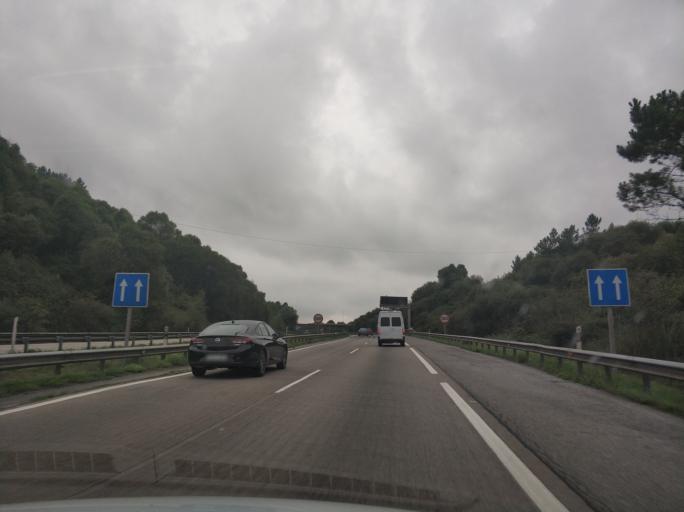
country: ES
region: Asturias
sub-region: Province of Asturias
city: Corvera de Asturias
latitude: 43.5069
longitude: -5.8067
